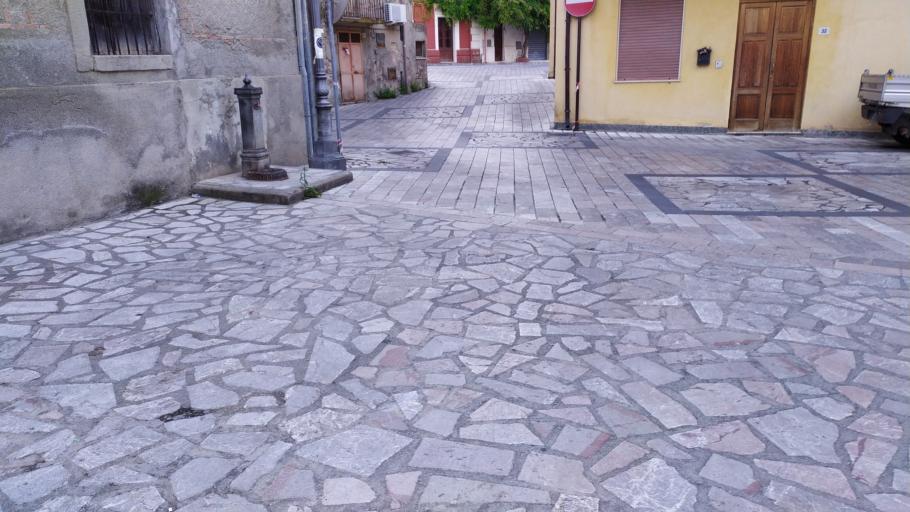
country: IT
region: Sicily
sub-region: Messina
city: Gualtieri Sicamino
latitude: 38.1628
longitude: 15.3163
